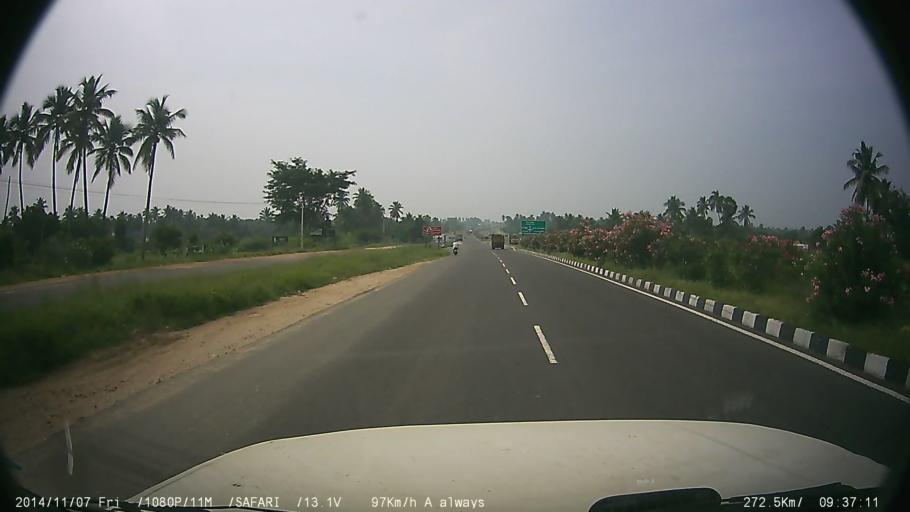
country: IN
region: Tamil Nadu
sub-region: Erode
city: Erode
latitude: 11.3579
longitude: 77.6455
